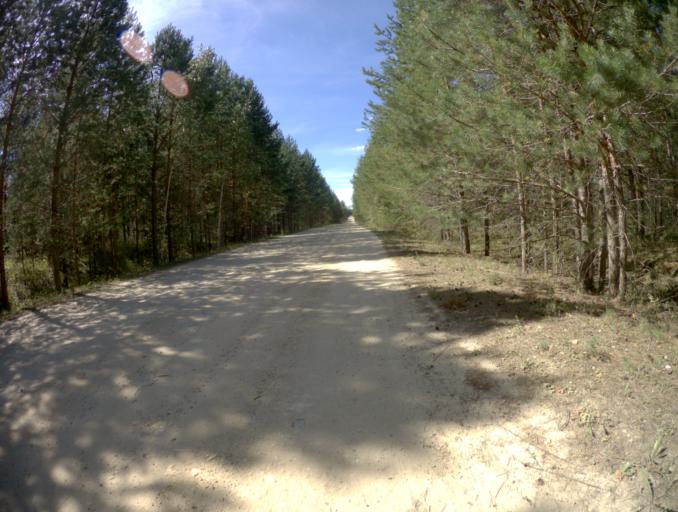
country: RU
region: Vladimir
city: Zolotkovo
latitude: 55.5956
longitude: 41.1757
